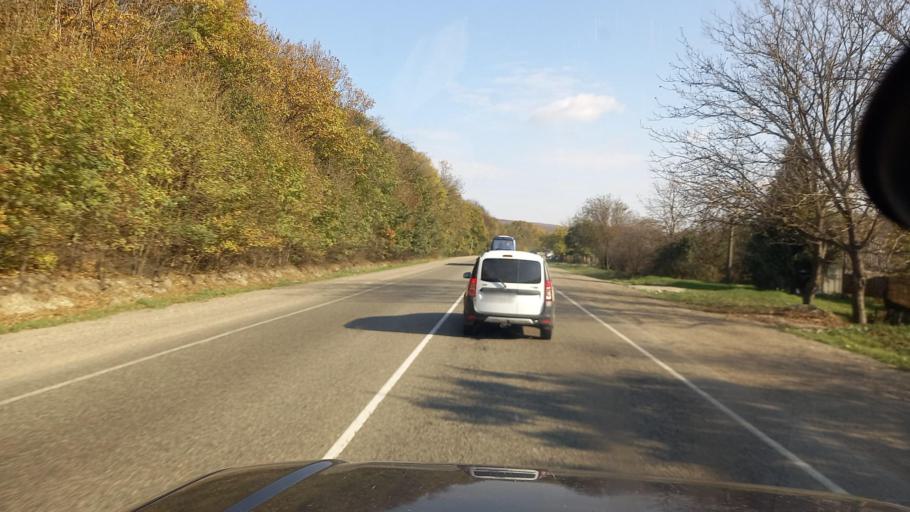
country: RU
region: Krasnodarskiy
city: Verkhnebakanskiy
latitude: 44.8544
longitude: 37.7303
